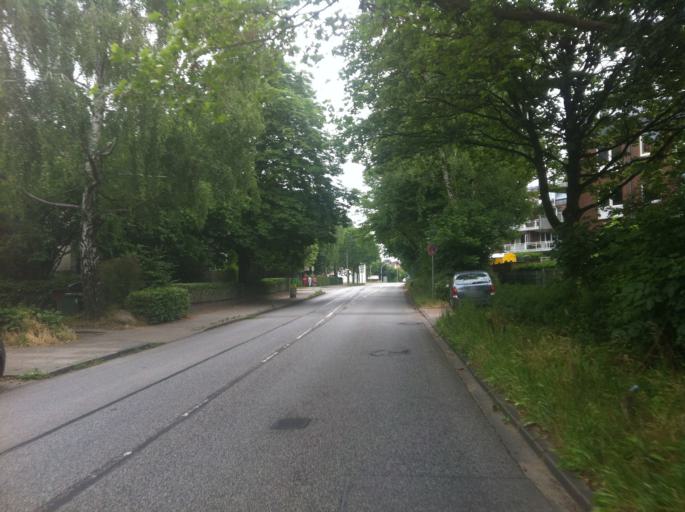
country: DE
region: Hamburg
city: Farmsen-Berne
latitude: 53.6064
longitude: 10.1346
